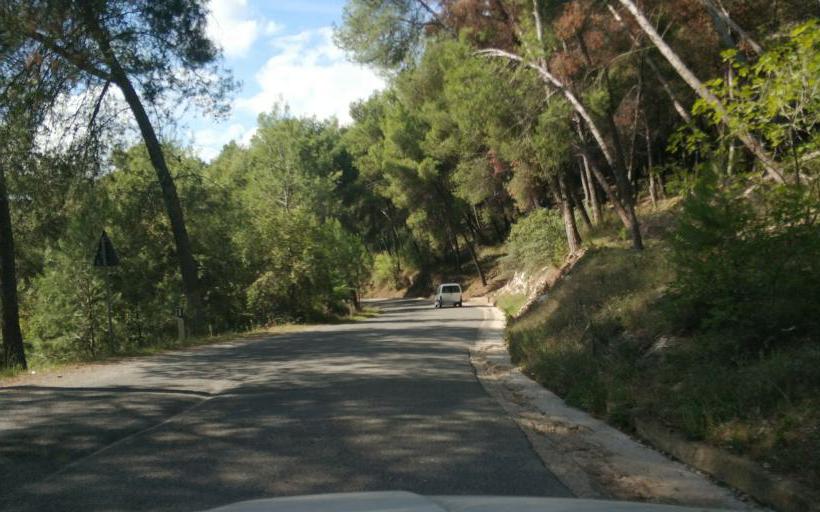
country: AL
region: Durres
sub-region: Rrethi i Krujes
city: Kruje
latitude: 41.4908
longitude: 19.7694
